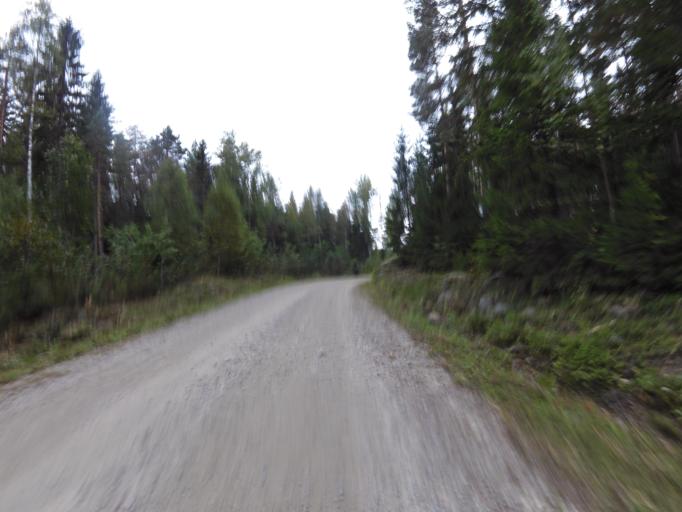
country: SE
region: Gaevleborg
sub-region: Sandvikens Kommun
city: Sandviken
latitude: 60.7563
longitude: 16.8477
